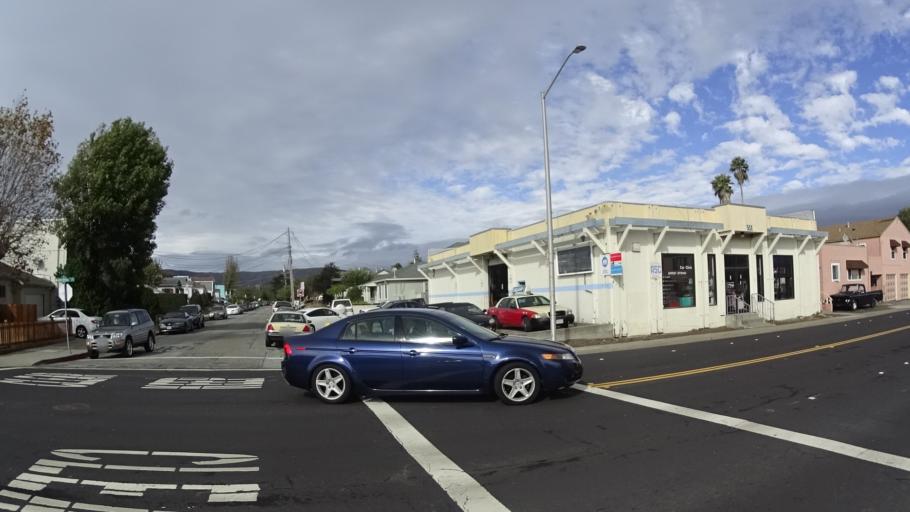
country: US
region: California
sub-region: San Mateo County
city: San Bruno
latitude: 37.6308
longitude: -122.4085
